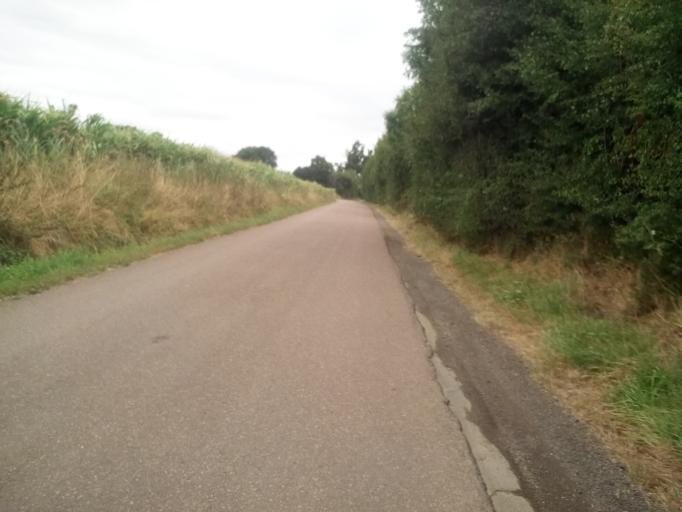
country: FR
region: Lower Normandy
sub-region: Departement du Calvados
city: Clinchamps-sur-Orne
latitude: 49.0389
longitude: -0.3935
